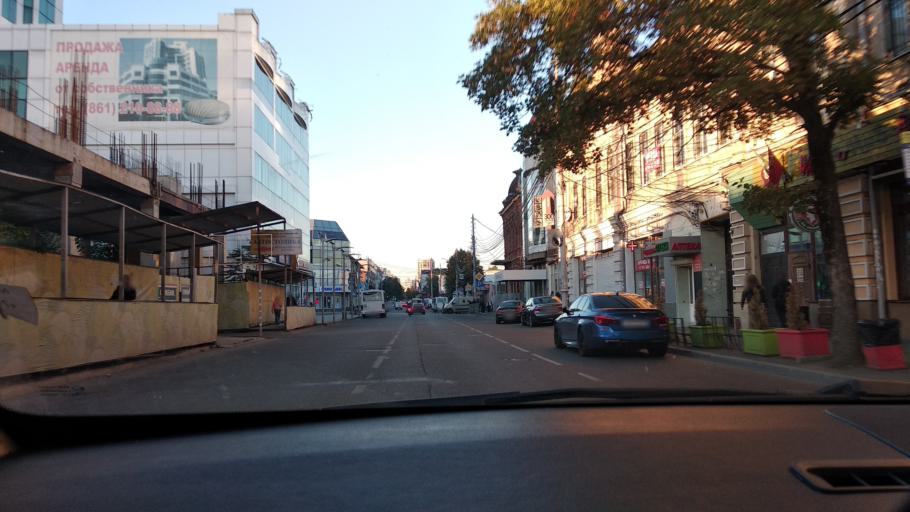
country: RU
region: Krasnodarskiy
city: Krasnodar
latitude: 45.0257
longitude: 38.9730
